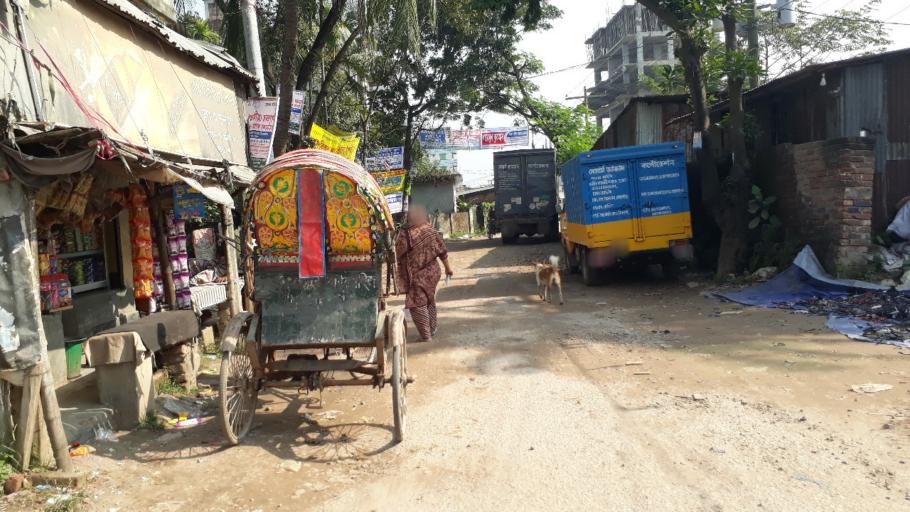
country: BD
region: Dhaka
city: Tungi
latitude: 23.8566
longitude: 90.2569
